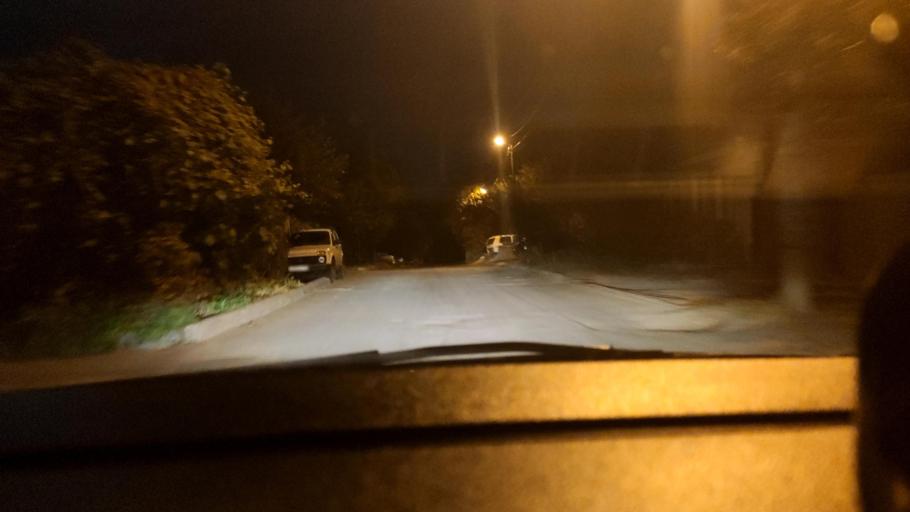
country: RU
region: Voronezj
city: Voronezh
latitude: 51.6277
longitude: 39.1921
